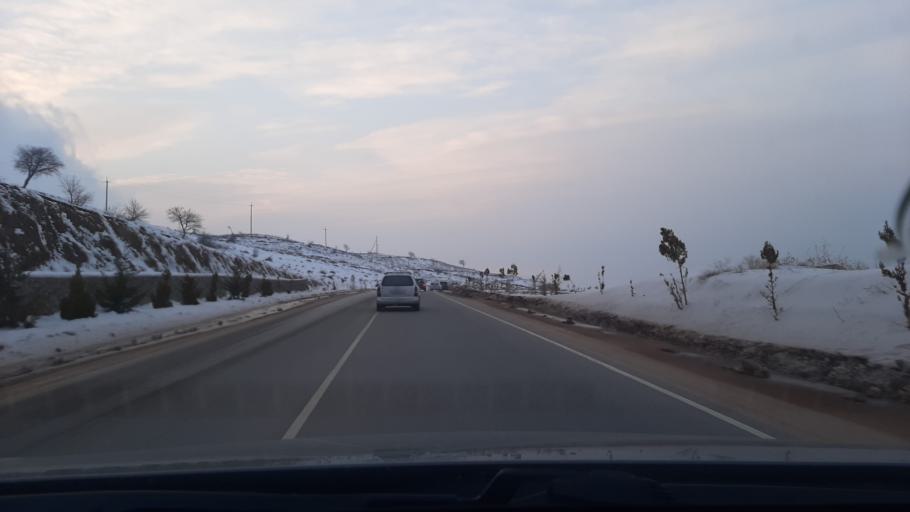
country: TJ
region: Republican Subordination
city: Vahdat
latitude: 38.4887
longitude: 69.1624
